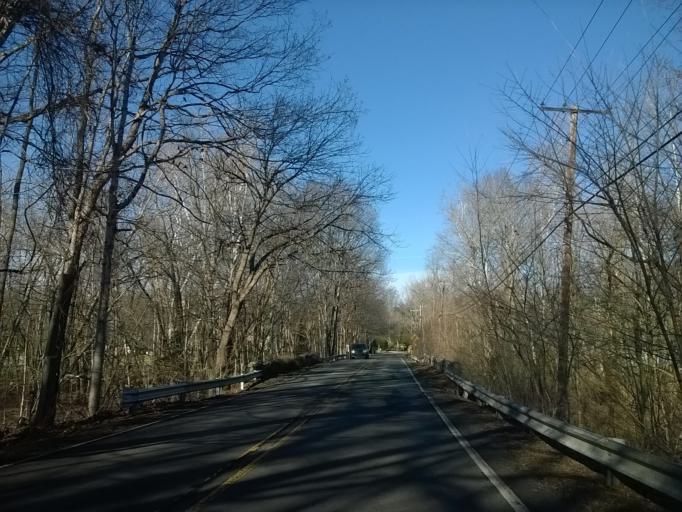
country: US
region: Indiana
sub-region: Marion County
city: Meridian Hills
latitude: 39.8991
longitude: -86.1650
